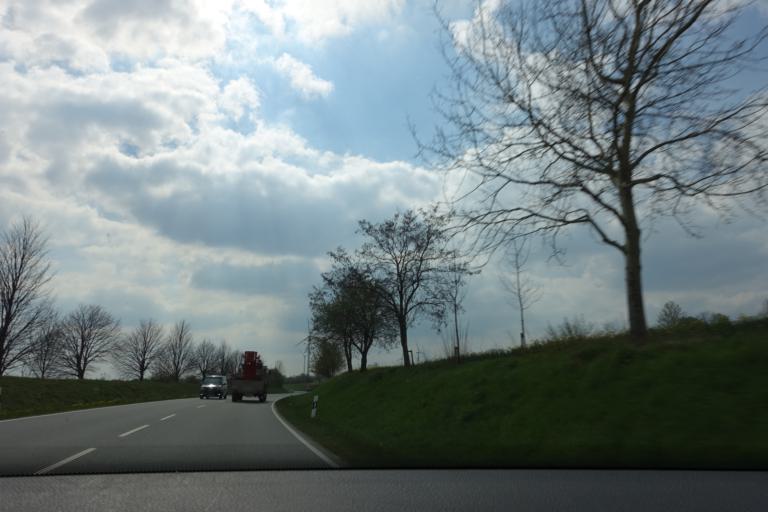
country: DE
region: Saxony
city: Gornau
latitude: 50.7559
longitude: 13.0488
